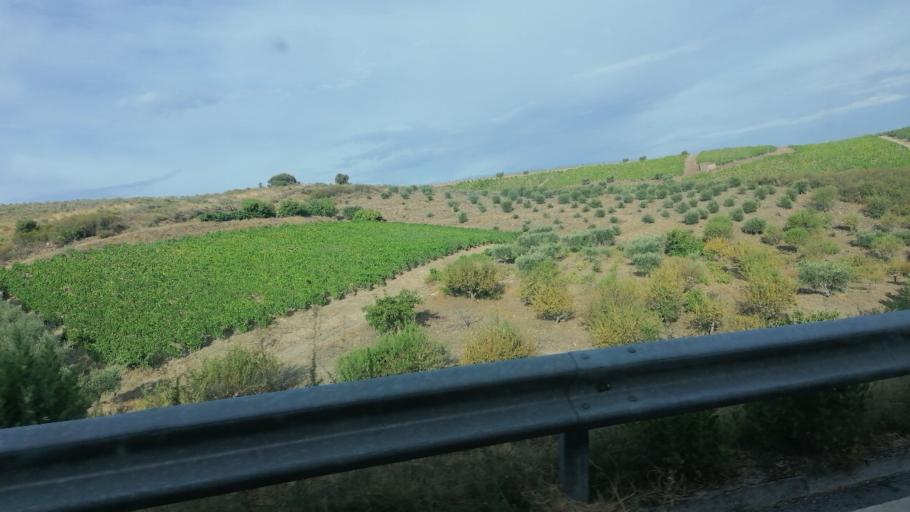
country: PT
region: Viseu
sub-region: Sao Joao da Pesqueira
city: Sao Joao da Pesqueira
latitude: 41.1300
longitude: -7.4370
